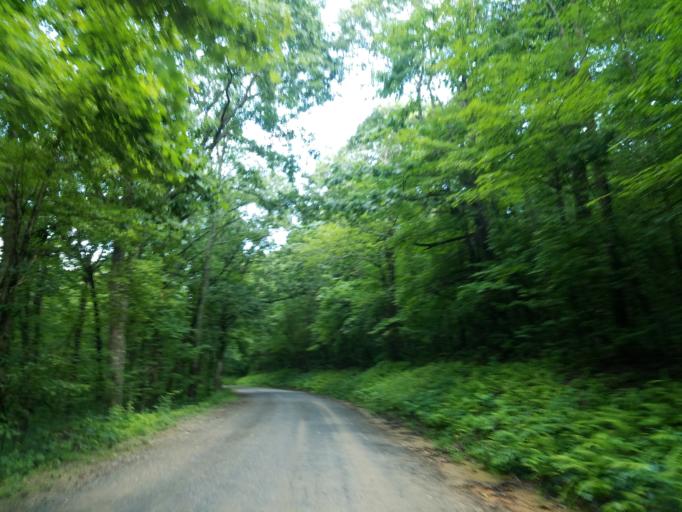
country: US
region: Georgia
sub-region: Dawson County
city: Dawsonville
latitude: 34.6334
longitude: -84.1856
